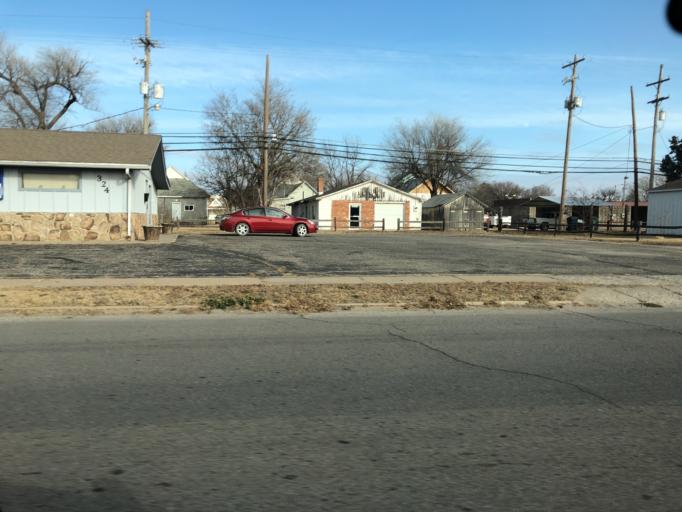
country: US
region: Kansas
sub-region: Reno County
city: Hutchinson
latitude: 38.0575
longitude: -97.9387
